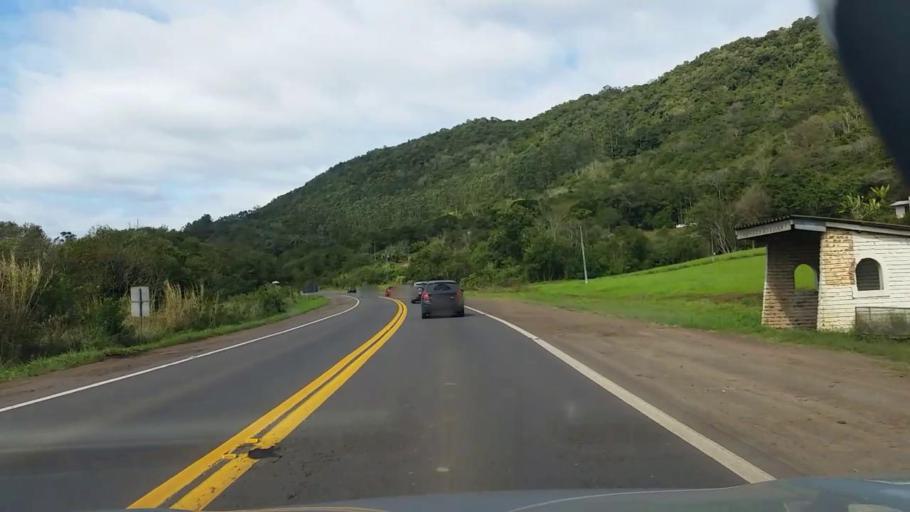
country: BR
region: Rio Grande do Sul
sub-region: Arroio Do Meio
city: Arroio do Meio
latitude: -29.3319
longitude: -52.1004
